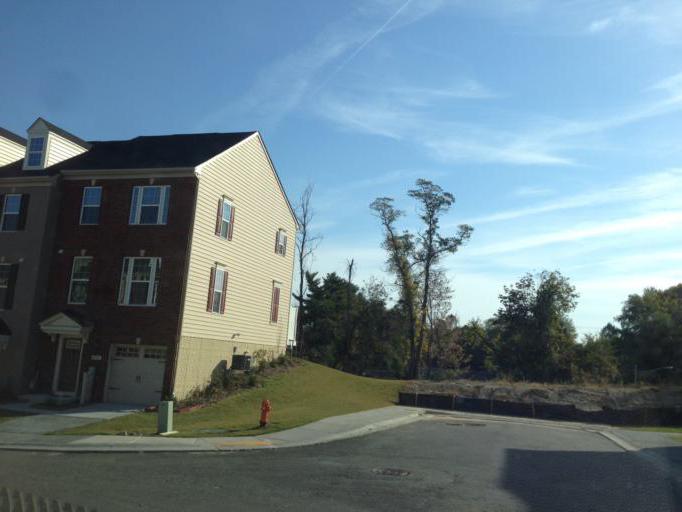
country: US
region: Maryland
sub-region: Howard County
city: Ellicott City
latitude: 39.2786
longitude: -76.8090
